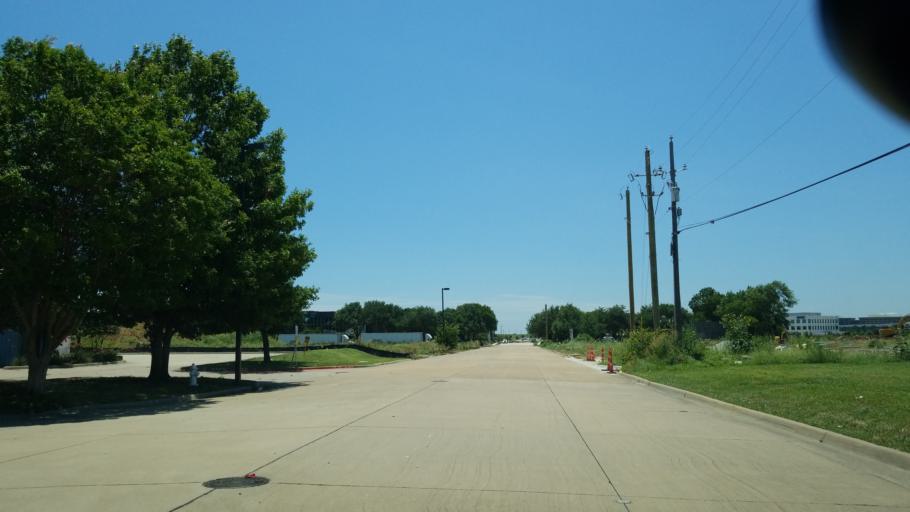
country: US
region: Texas
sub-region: Dallas County
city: Farmers Branch
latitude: 32.9212
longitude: -96.9121
